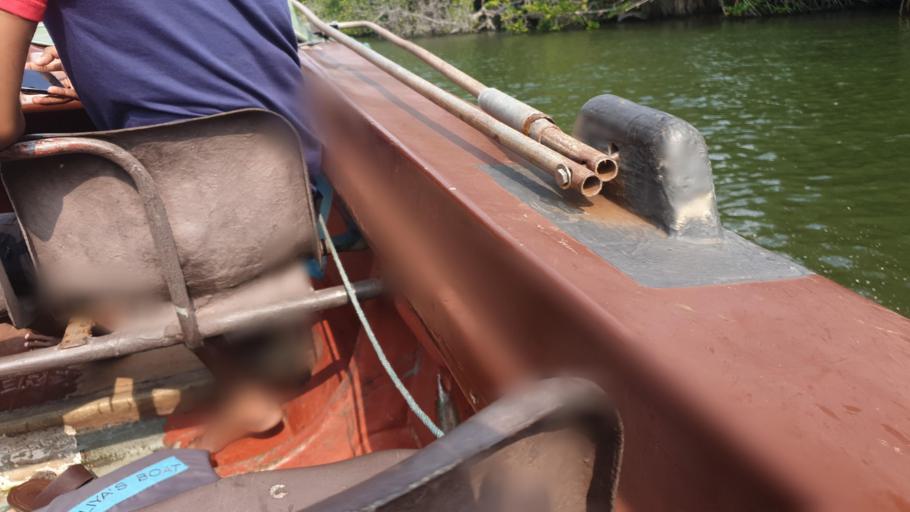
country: LK
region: Southern
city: Ambalangoda
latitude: 6.2752
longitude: 80.0422
